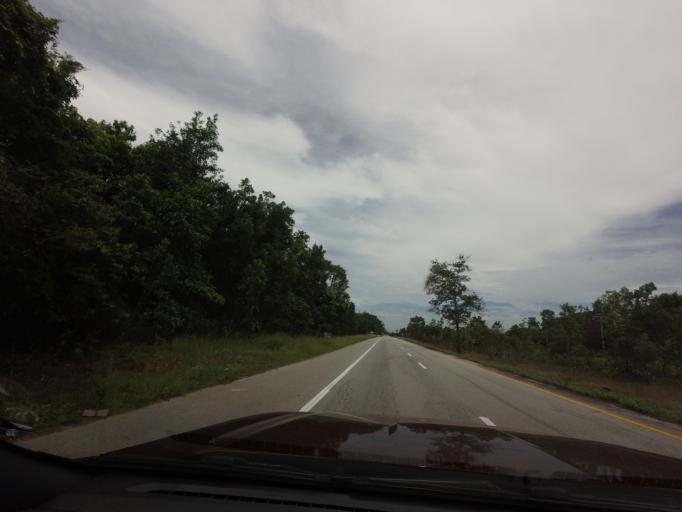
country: TH
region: Narathiwat
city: Narathiwat
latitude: 6.3492
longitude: 101.8870
